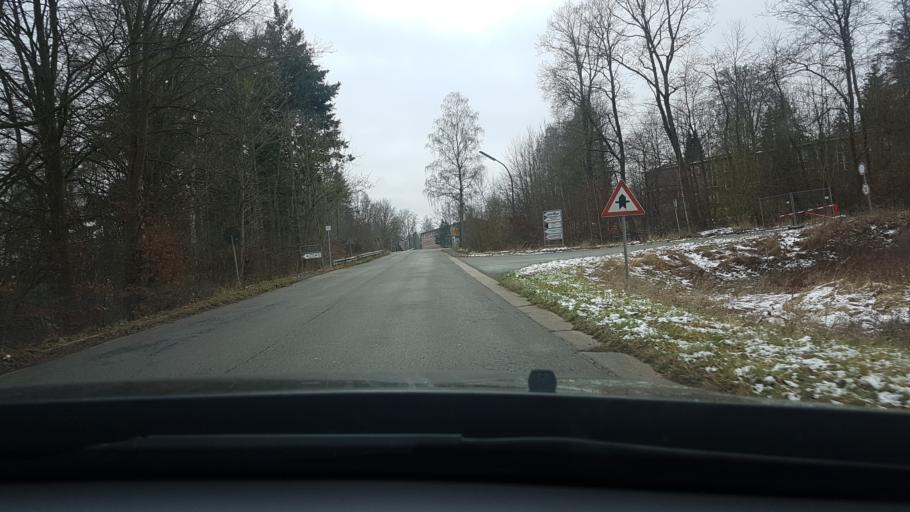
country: DE
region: Hesse
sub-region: Regierungsbezirk Kassel
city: Wolfhagen
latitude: 51.3380
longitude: 9.1272
